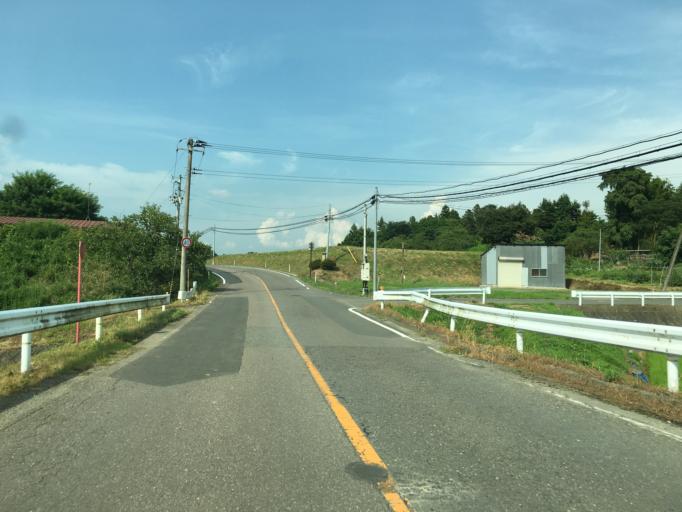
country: JP
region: Fukushima
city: Koriyama
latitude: 37.3483
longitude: 140.4129
